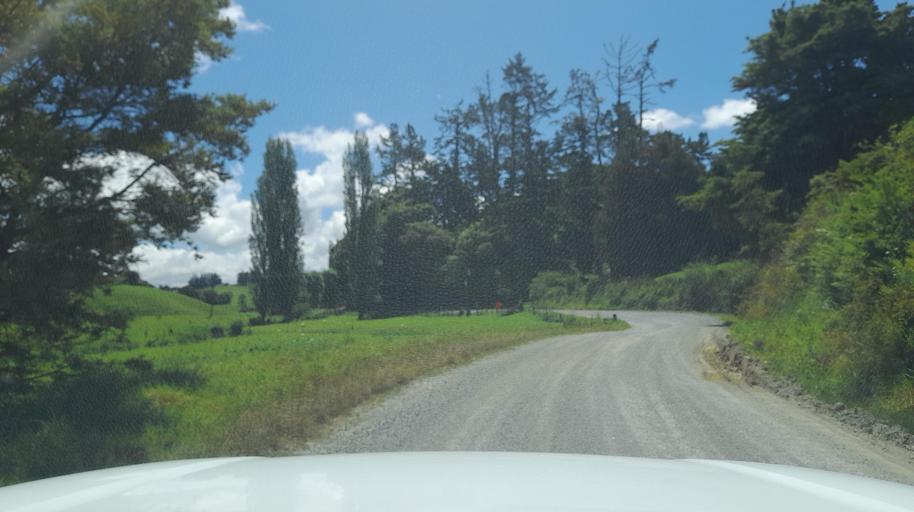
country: NZ
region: Northland
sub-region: Far North District
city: Kaitaia
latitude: -35.1206
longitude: 173.3986
